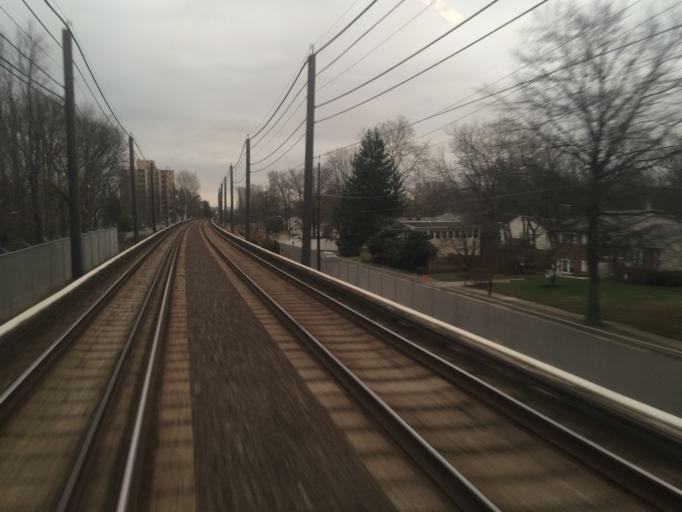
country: US
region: New Jersey
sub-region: Camden County
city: Collingswood
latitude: 39.9100
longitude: -75.0534
